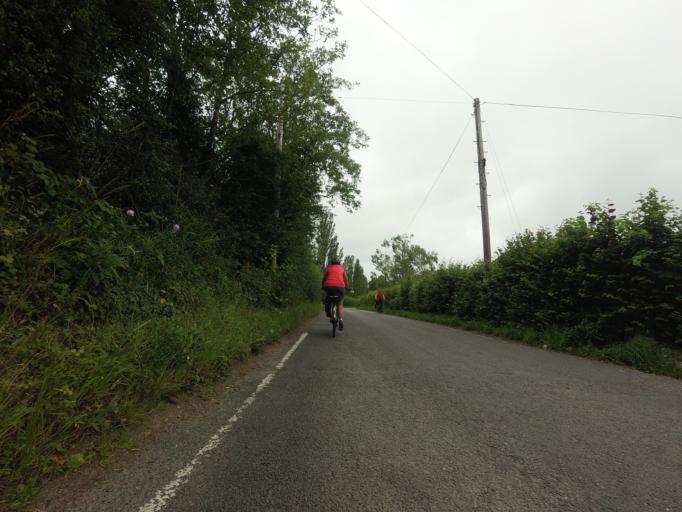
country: GB
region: England
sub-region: Kent
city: West Malling
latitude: 51.2898
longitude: 0.3953
